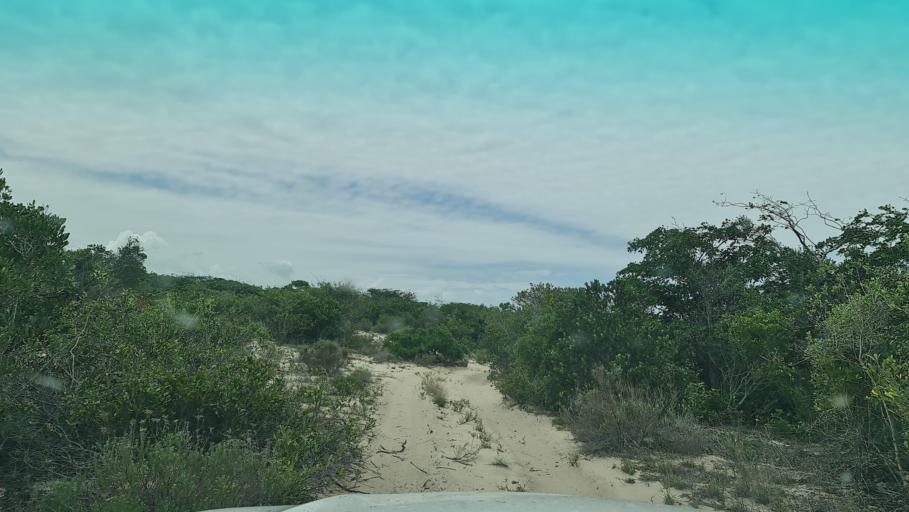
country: MZ
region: Maputo
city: Manhica
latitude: -25.6327
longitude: 32.7867
